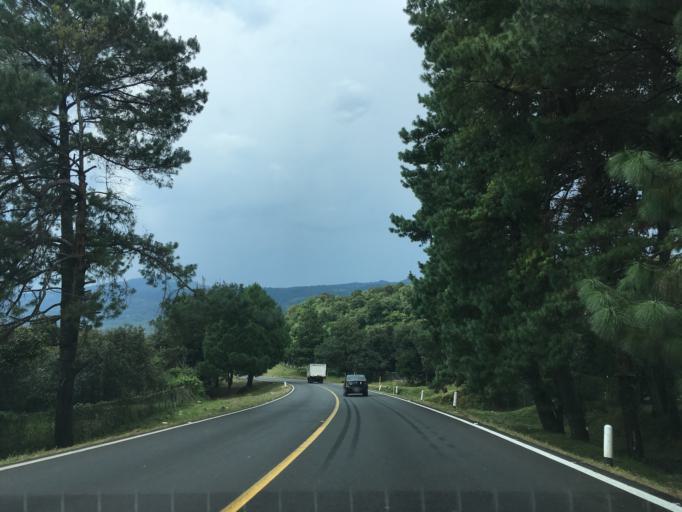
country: MX
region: Michoacan
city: Tingambato
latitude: 19.5000
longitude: -101.8400
